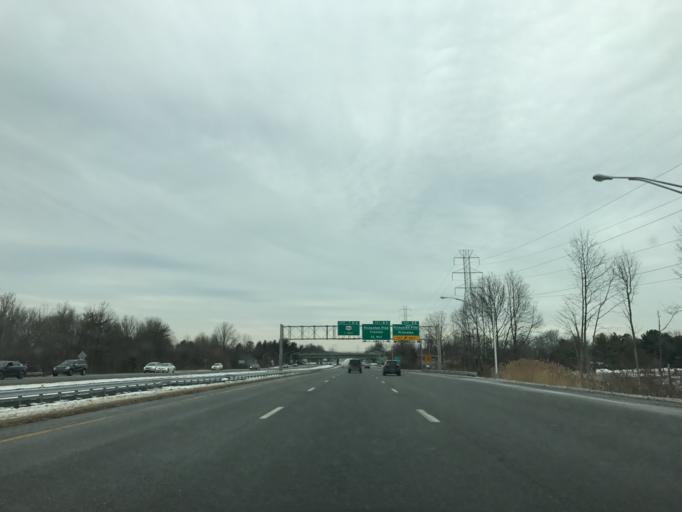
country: US
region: New Jersey
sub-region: Mercer County
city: Lawrenceville
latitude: 40.2865
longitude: -74.7081
